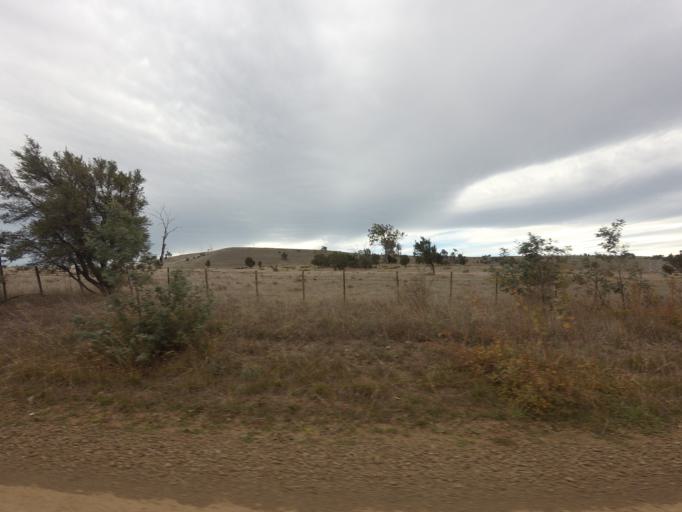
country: AU
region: Tasmania
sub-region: Derwent Valley
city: New Norfolk
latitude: -42.5591
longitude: 146.9199
